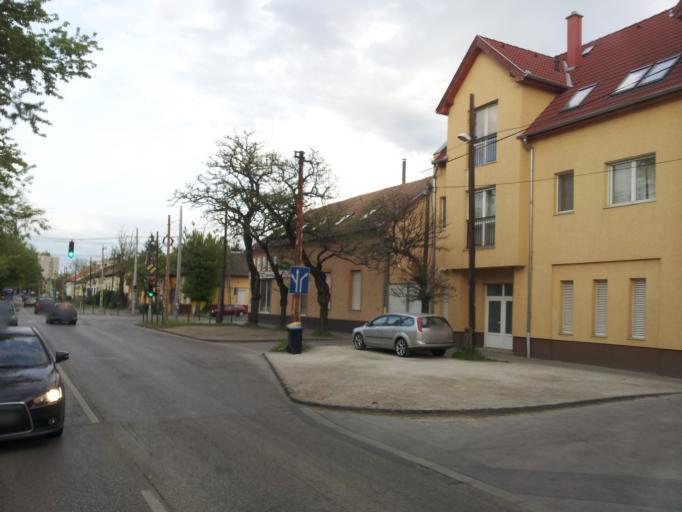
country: HU
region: Budapest
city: Budapest XV. keruelet
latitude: 47.5656
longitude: 19.1225
